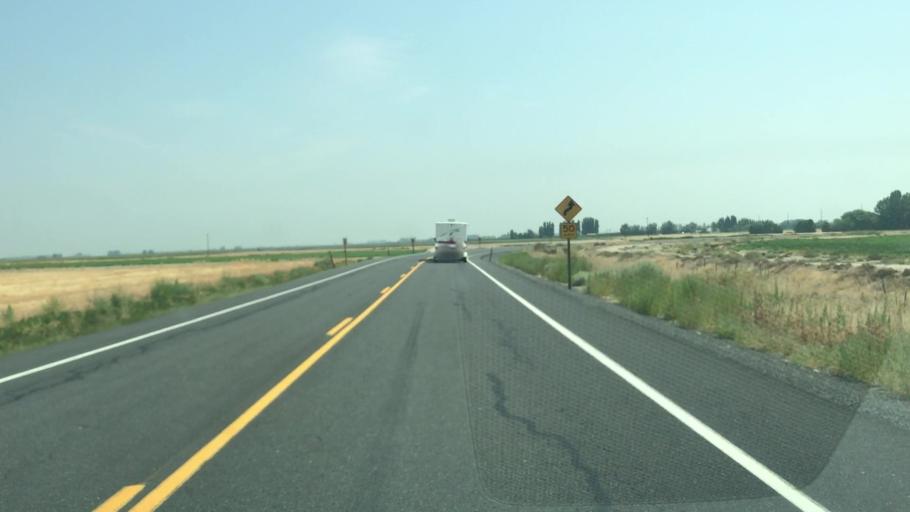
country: US
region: Washington
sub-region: Grant County
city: Quincy
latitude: 47.1638
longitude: -119.9231
